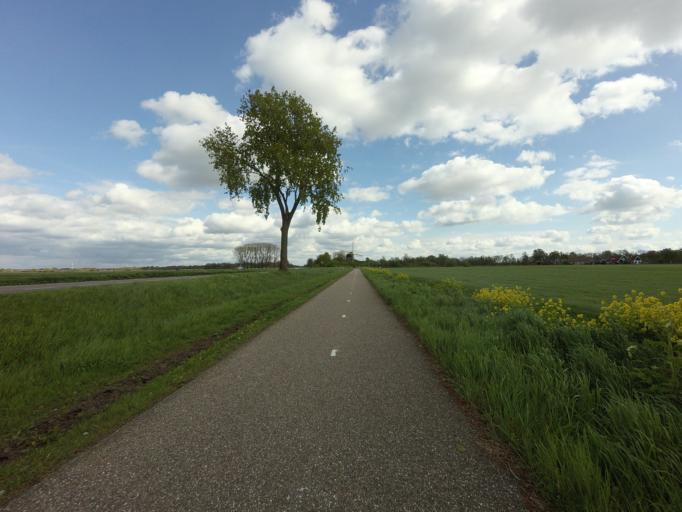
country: NL
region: Utrecht
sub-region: Stichtse Vecht
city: Vreeland
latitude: 52.2384
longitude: 5.0543
